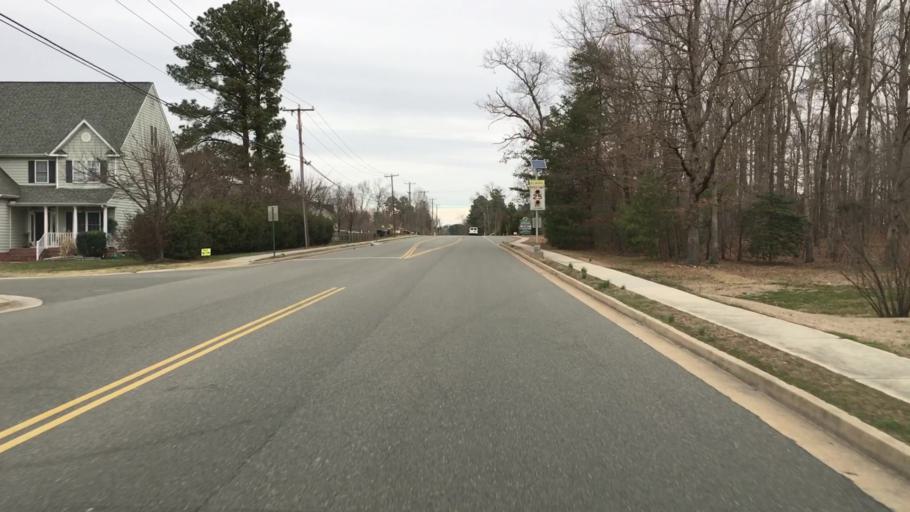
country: US
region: Virginia
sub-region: Henrico County
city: Laurel
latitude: 37.6578
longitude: -77.5454
